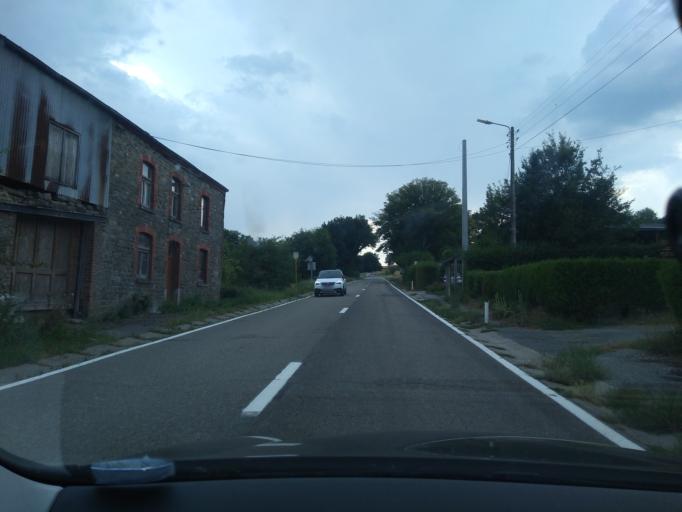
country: BE
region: Wallonia
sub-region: Province du Luxembourg
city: Bertogne
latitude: 50.0697
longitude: 5.6367
